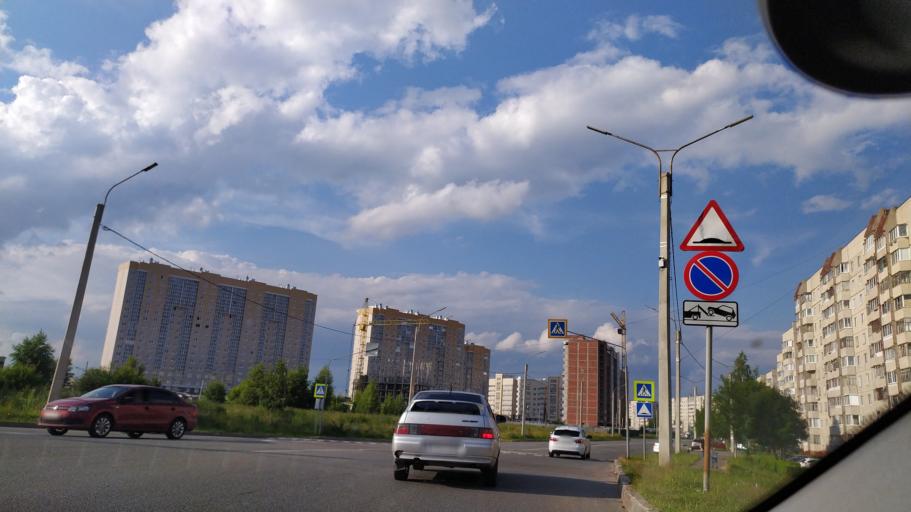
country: RU
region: Chuvashia
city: Novocheboksarsk
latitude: 56.1136
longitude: 47.4402
